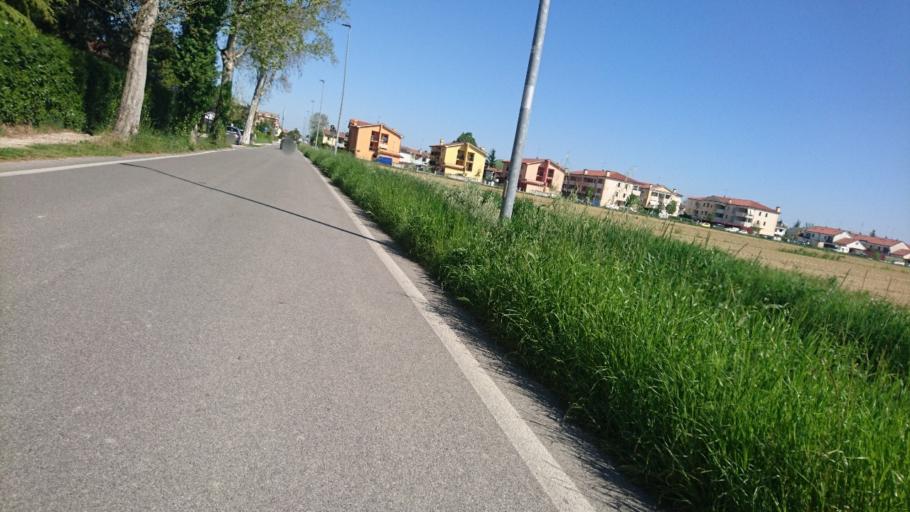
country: IT
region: Veneto
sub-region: Provincia di Venezia
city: Marcon-Gaggio-Colmello
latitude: 45.5618
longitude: 12.2923
